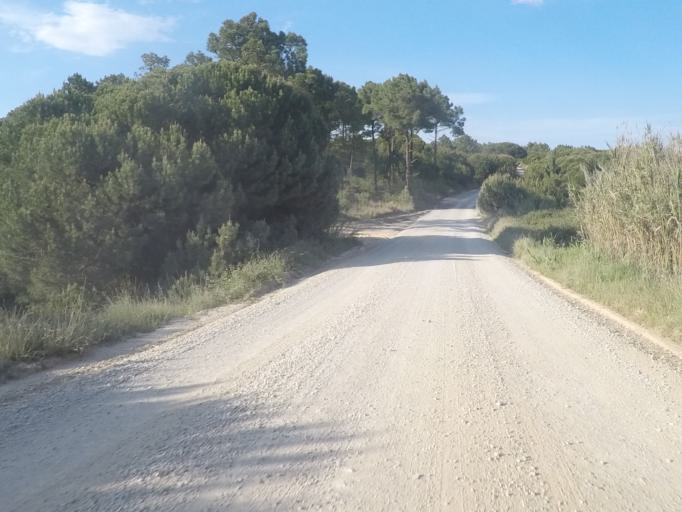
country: PT
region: Setubal
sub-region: Sesimbra
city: Sesimbra
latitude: 38.4569
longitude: -9.1884
